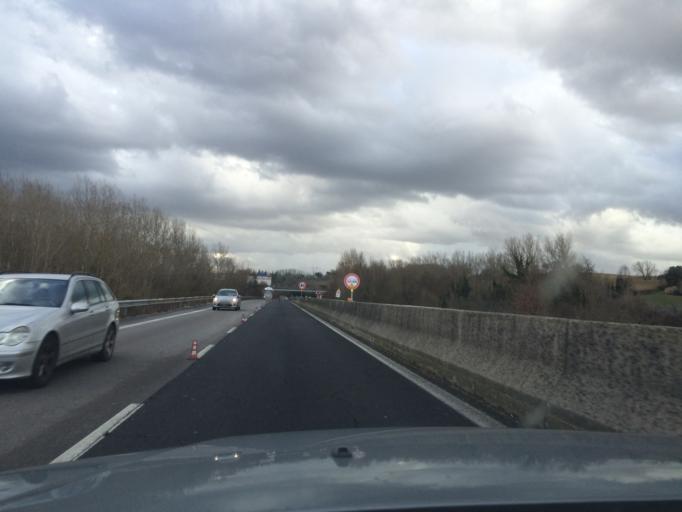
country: IT
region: Umbria
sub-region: Provincia di Terni
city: San Gemini
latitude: 42.6400
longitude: 12.5425
